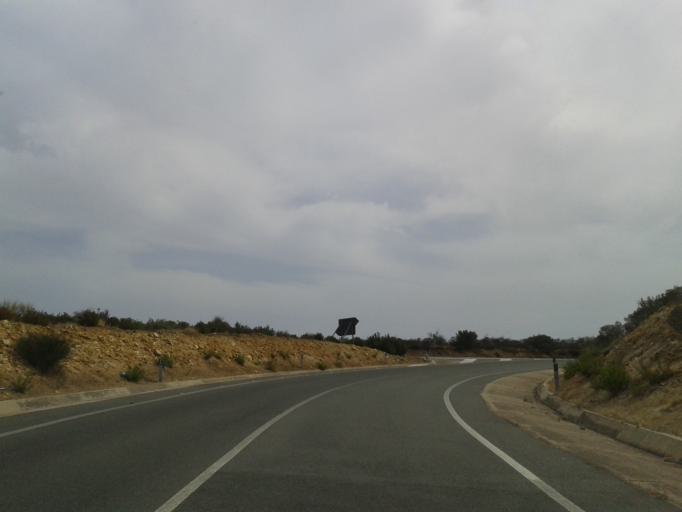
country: IT
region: Sardinia
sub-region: Provincia di Cagliari
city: Castiadas
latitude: 39.2355
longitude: 9.5119
